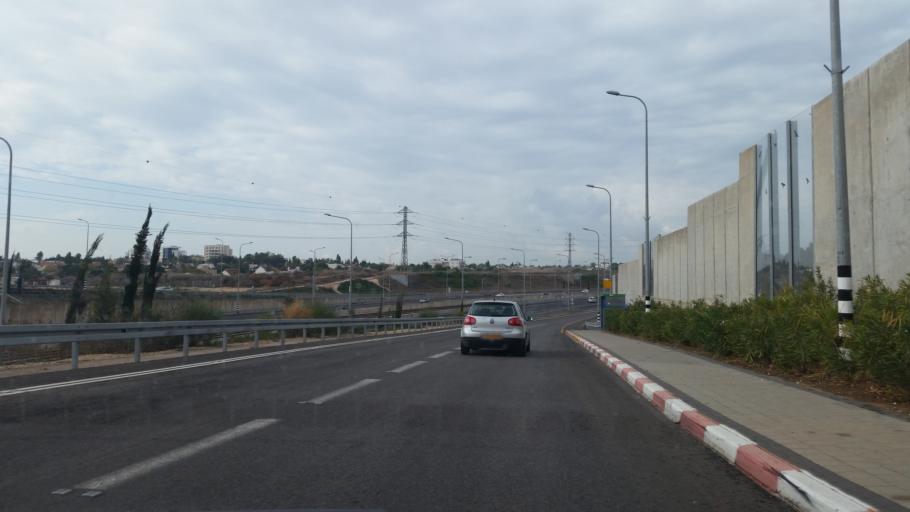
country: IL
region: Central District
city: Ra'anana
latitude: 32.1724
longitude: 34.8679
